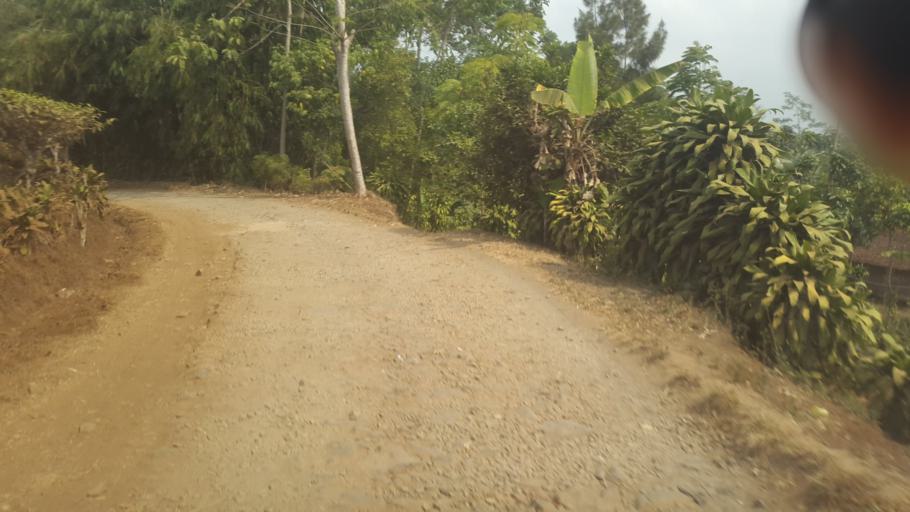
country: ID
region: West Java
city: Nyalindung
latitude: -7.0488
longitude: 106.9303
